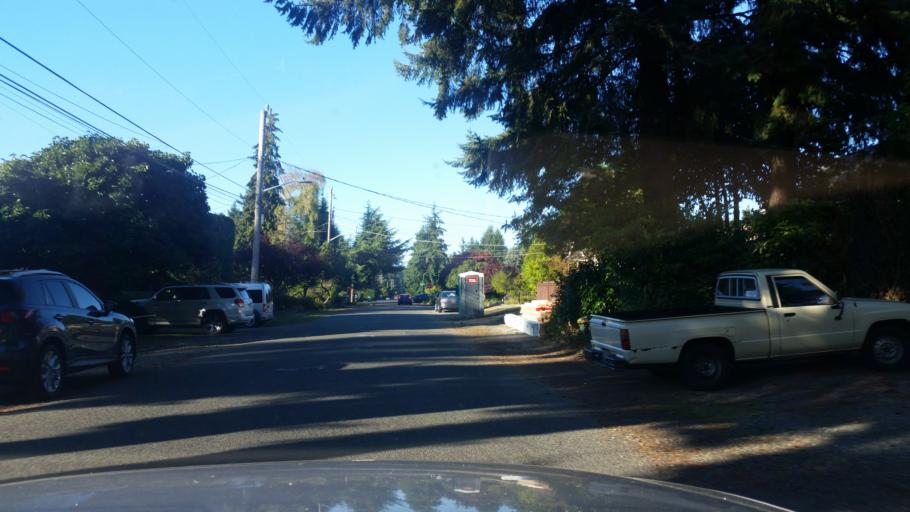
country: US
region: Washington
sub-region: King County
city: Shoreline
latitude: 47.7186
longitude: -122.3623
